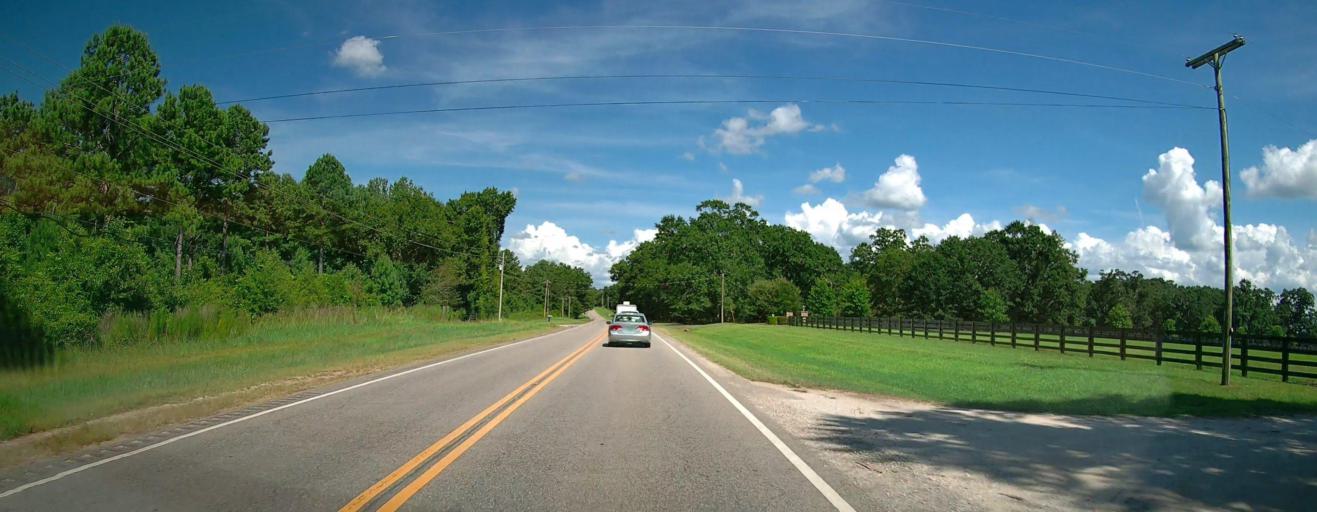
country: US
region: Alabama
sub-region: Elmore County
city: Tallassee
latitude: 32.3803
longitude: -85.8715
